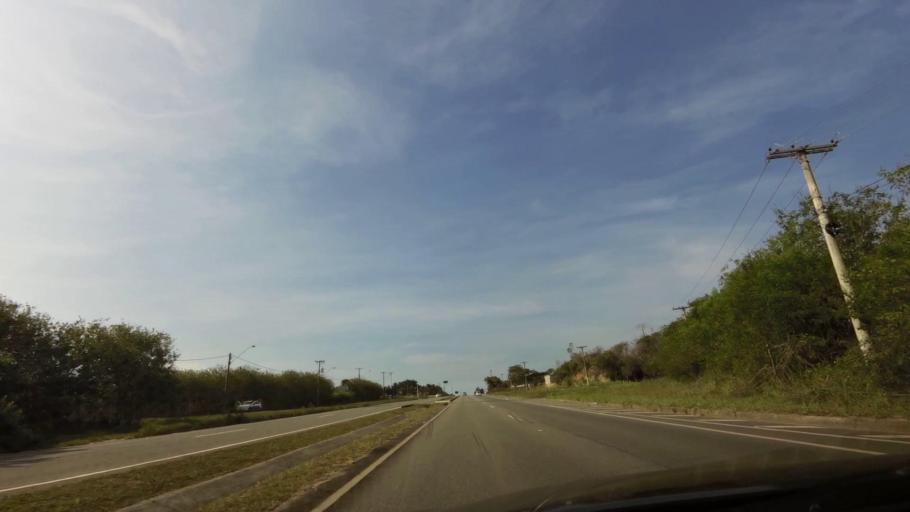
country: BR
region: Espirito Santo
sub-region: Guarapari
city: Guarapari
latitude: -20.5256
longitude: -40.3770
